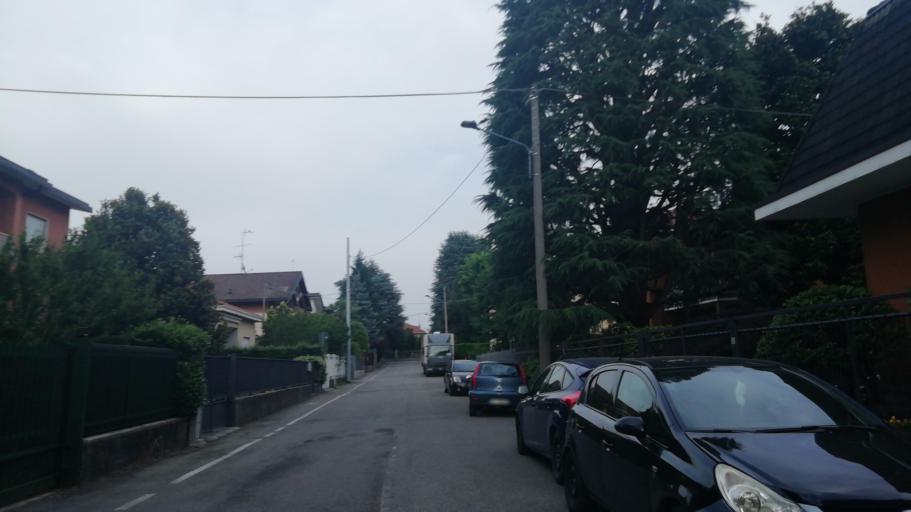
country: IT
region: Lombardy
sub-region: Provincia di Lecco
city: Osnago
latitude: 45.6822
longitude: 9.3937
